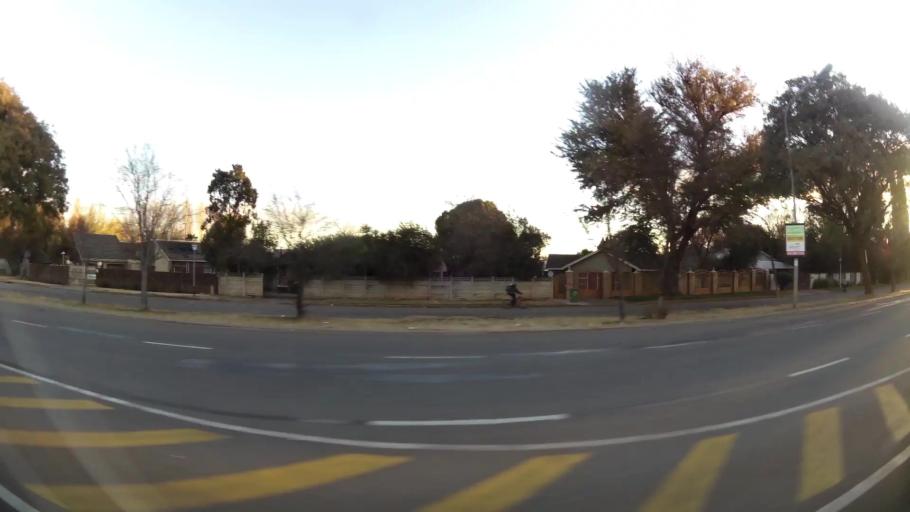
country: ZA
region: North-West
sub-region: Dr Kenneth Kaunda District Municipality
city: Potchefstroom
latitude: -26.7134
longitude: 27.1113
